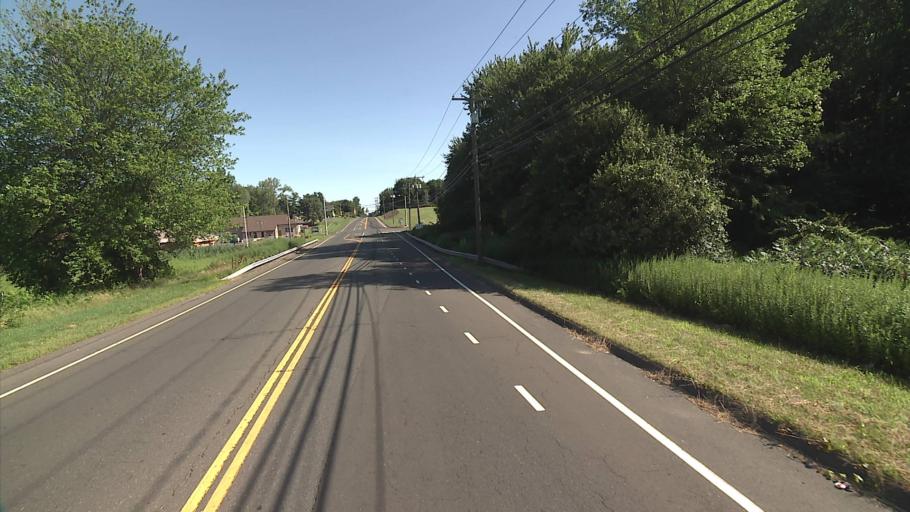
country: US
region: Connecticut
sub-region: New Haven County
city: Cheshire Village
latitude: 41.5475
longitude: -72.8916
